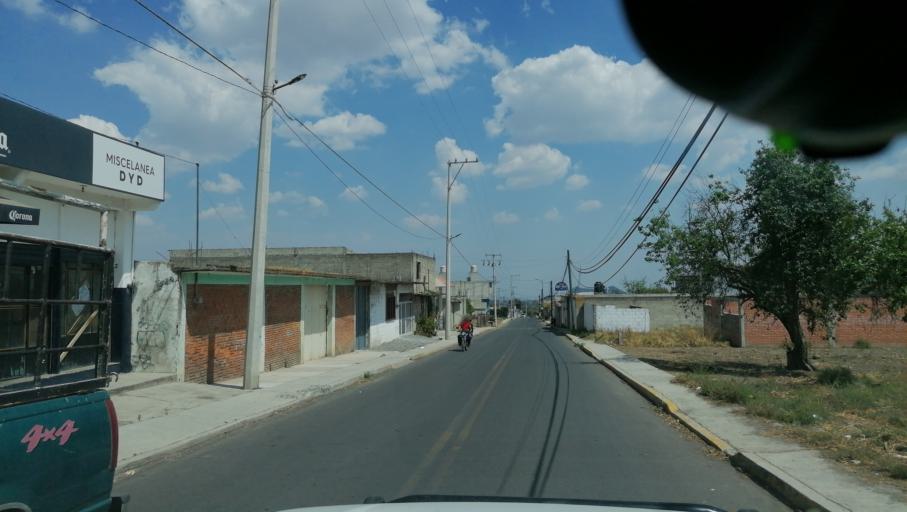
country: MX
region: Puebla
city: San Andres Calpan
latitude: 19.1034
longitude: -98.4754
